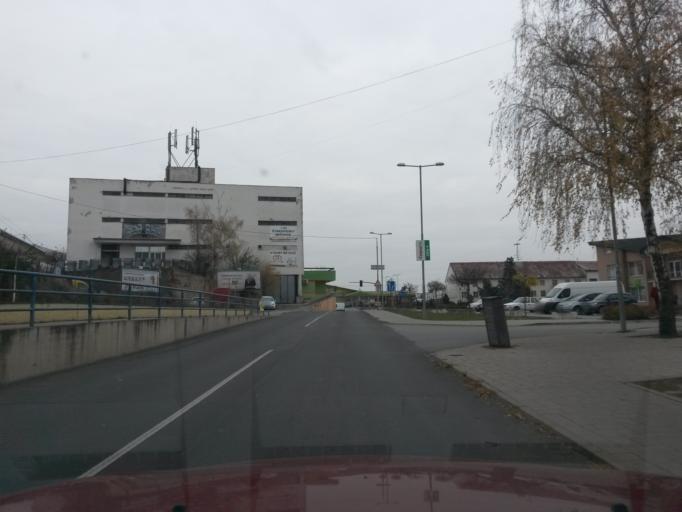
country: SK
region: Kosicky
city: Secovce
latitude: 48.7013
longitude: 21.6549
